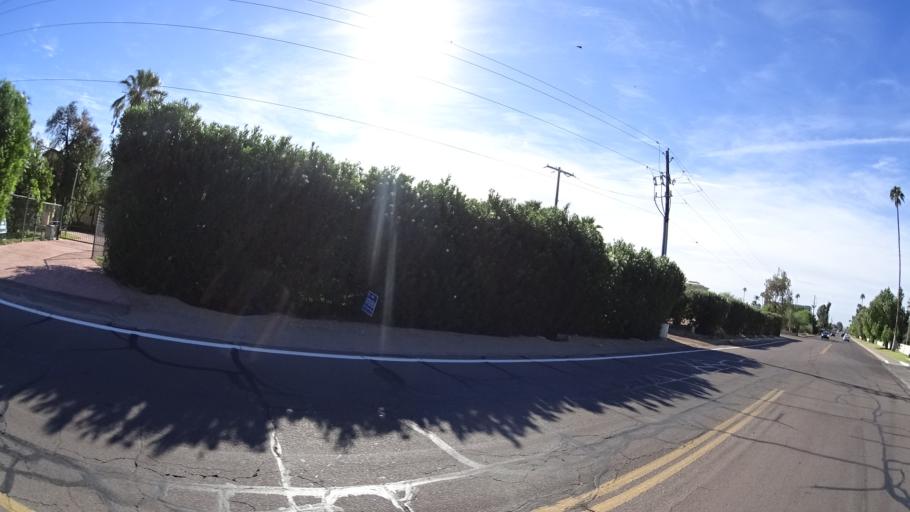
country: US
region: Arizona
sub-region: Maricopa County
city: Paradise Valley
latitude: 33.5079
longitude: -111.9347
